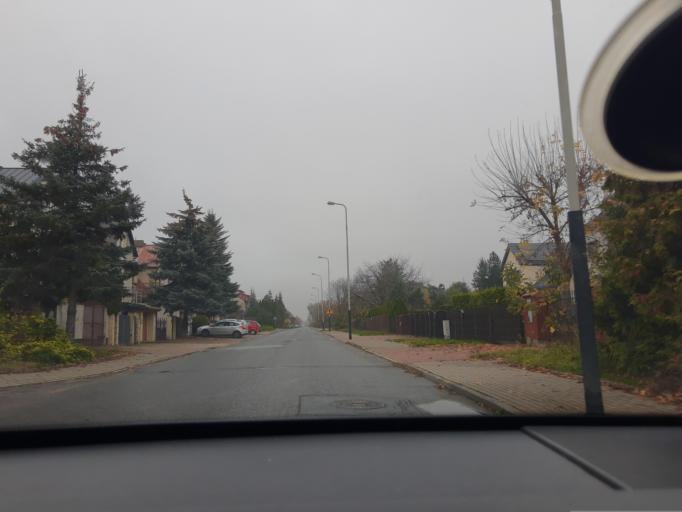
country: PL
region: Lodz Voivodeship
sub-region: Powiat pabianicki
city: Konstantynow Lodzki
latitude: 51.7387
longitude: 19.3798
